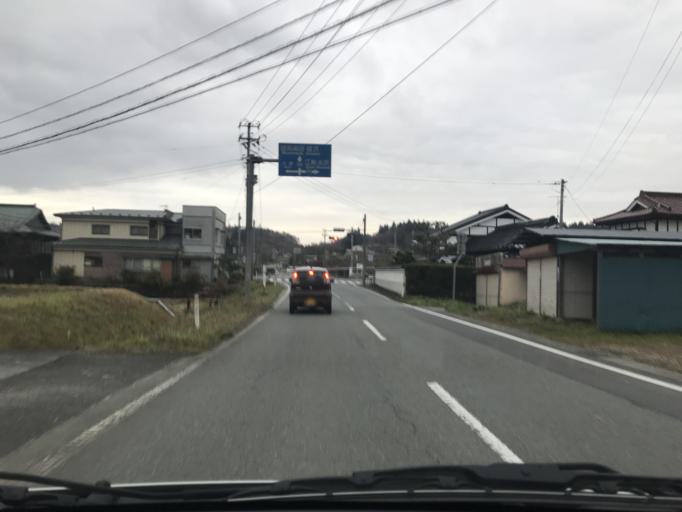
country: JP
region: Iwate
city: Ichinoseki
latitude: 39.0217
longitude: 141.3306
